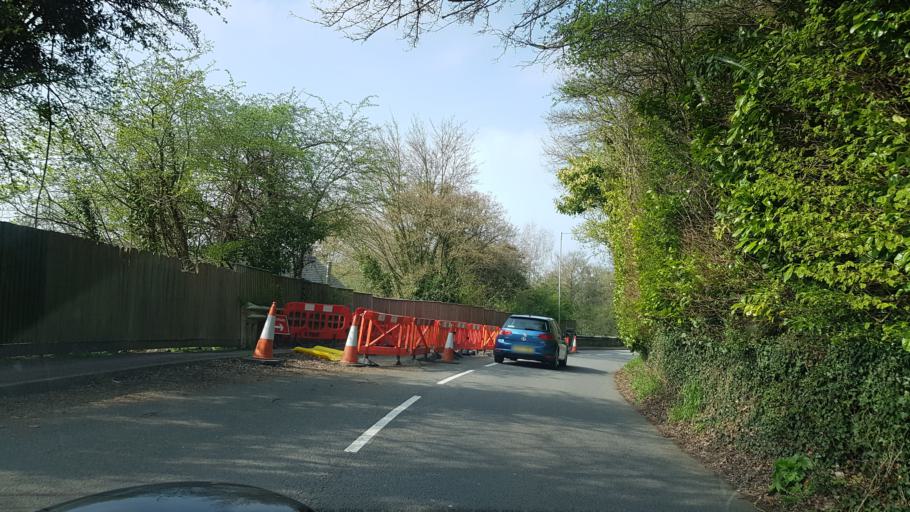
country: GB
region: Wales
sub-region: Monmouthshire
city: Monmouth
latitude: 51.8061
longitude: -2.7063
